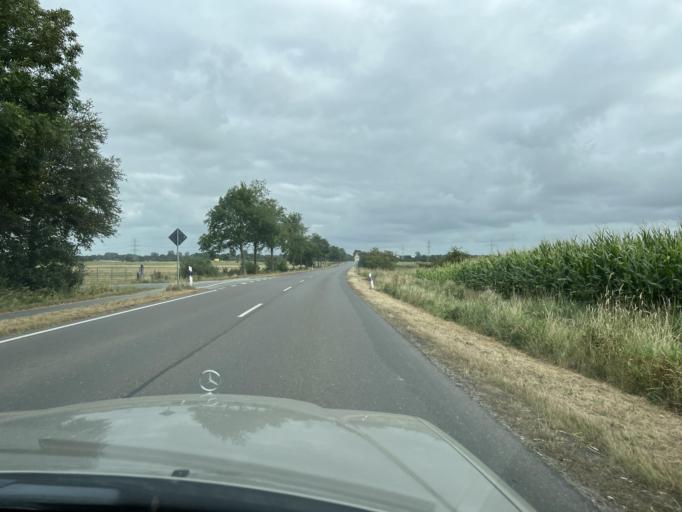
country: DE
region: Schleswig-Holstein
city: Stelle-Wittenwurth
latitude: 54.2507
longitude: 9.0658
